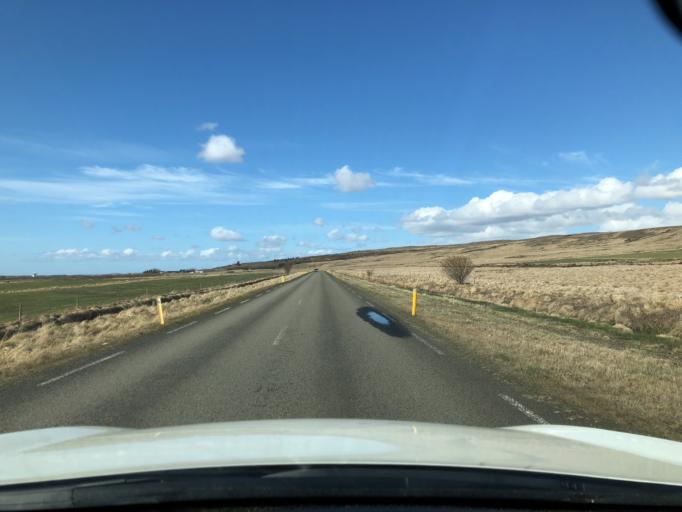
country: IS
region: West
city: Borgarnes
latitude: 64.6669
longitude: -21.3442
